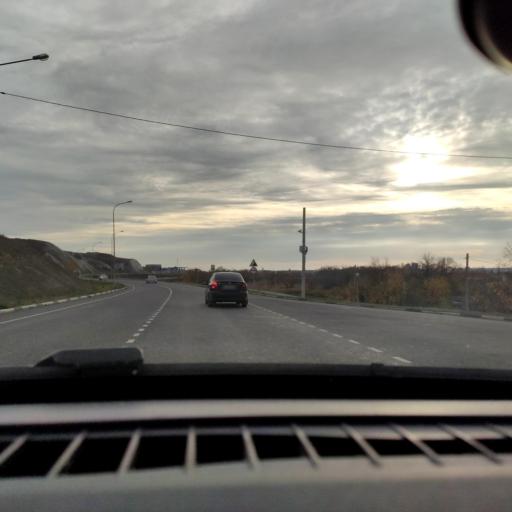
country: RU
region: Belgorod
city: Alekseyevka
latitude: 50.6414
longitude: 38.6585
